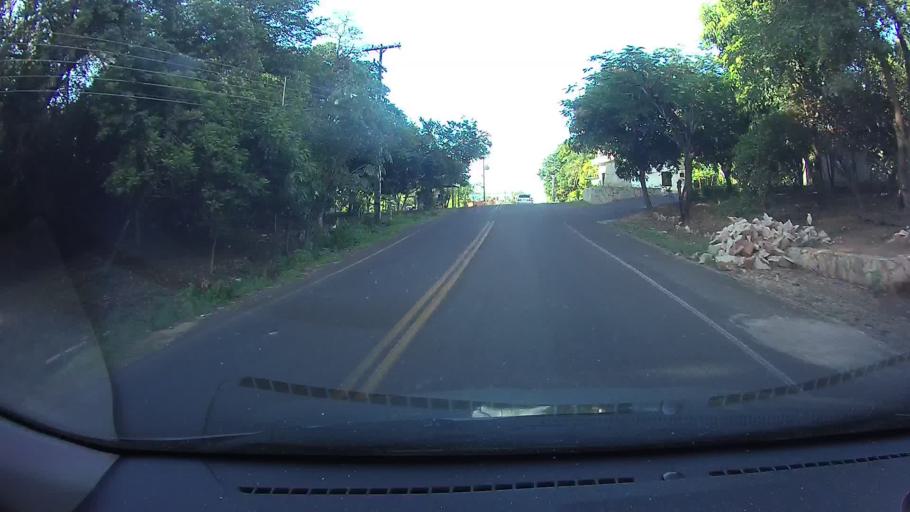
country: PY
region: Cordillera
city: Altos
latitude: -25.1807
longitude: -57.2310
